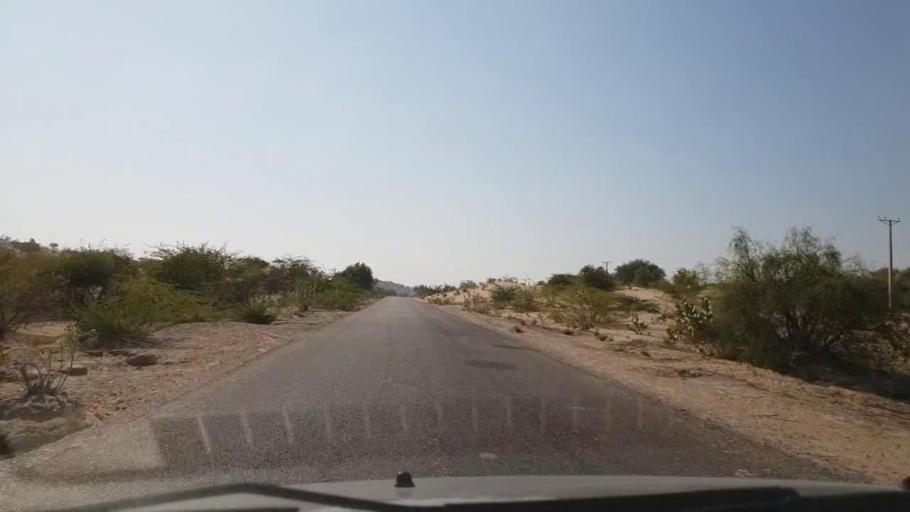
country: PK
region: Sindh
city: Diplo
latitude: 24.5648
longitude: 69.6754
